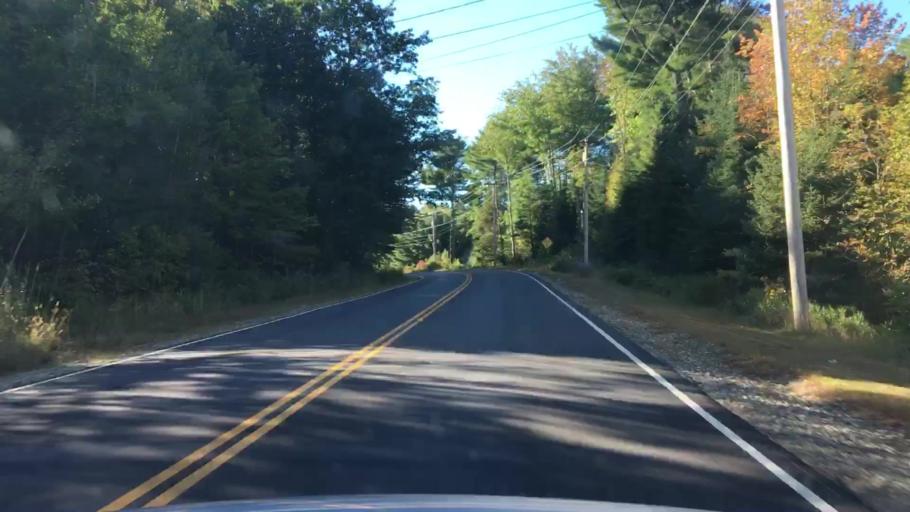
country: US
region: Maine
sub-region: Androscoggin County
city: Lisbon
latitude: 44.0742
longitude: -70.0993
